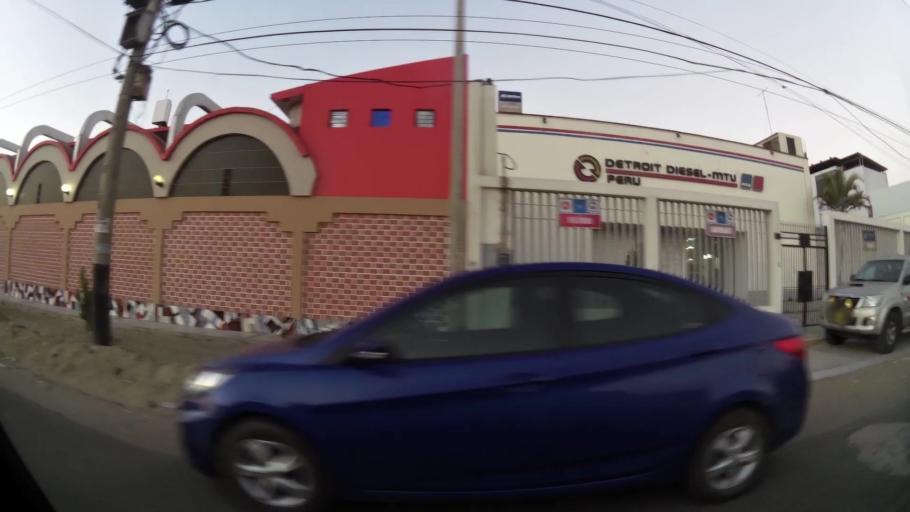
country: PE
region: Ancash
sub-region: Provincia de Santa
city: Buenos Aires
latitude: -9.1237
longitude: -78.5360
